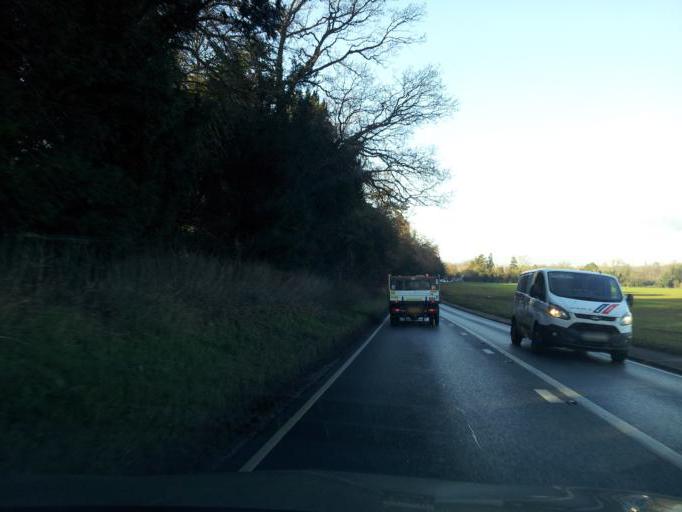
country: GB
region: England
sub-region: Suffolk
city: Bury St Edmunds
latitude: 52.2250
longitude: 0.7350
